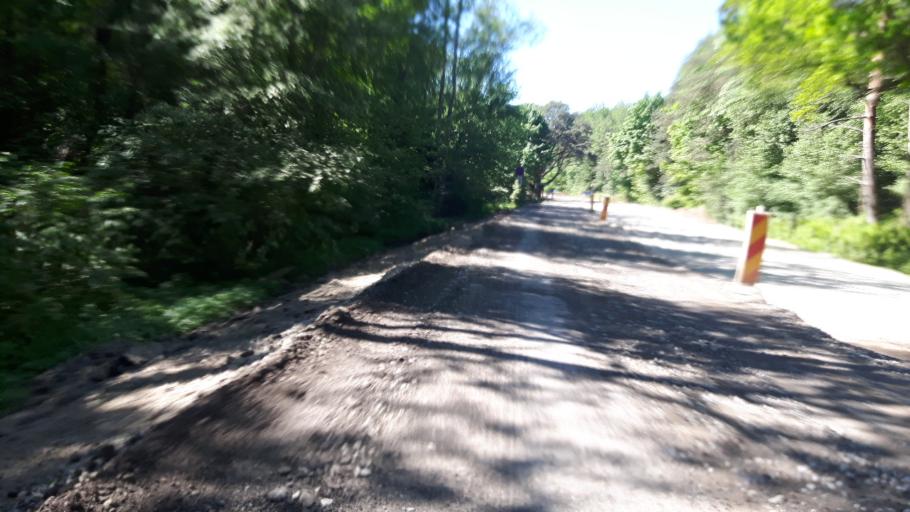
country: EE
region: Ida-Virumaa
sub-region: Narva-Joesuu linn
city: Narva-Joesuu
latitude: 59.4162
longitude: 27.9643
